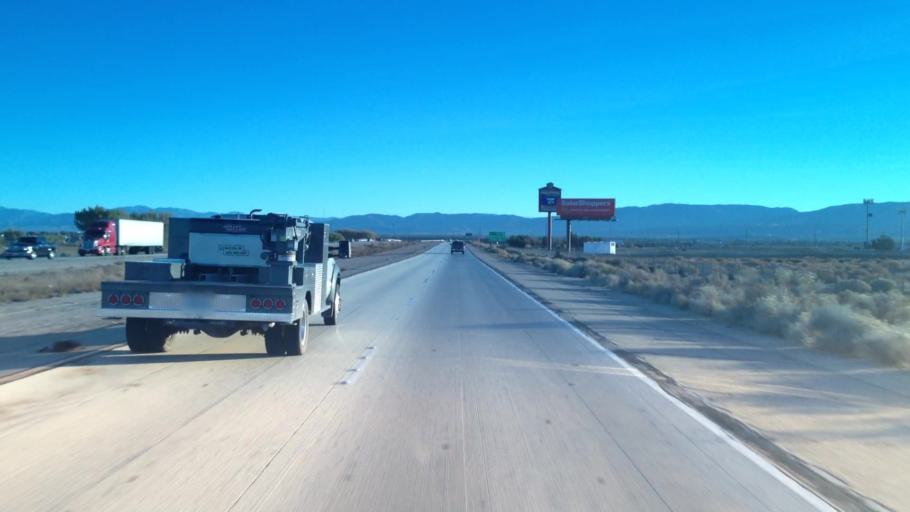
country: US
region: California
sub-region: Los Angeles County
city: Lancaster
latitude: 34.7275
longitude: -118.1705
